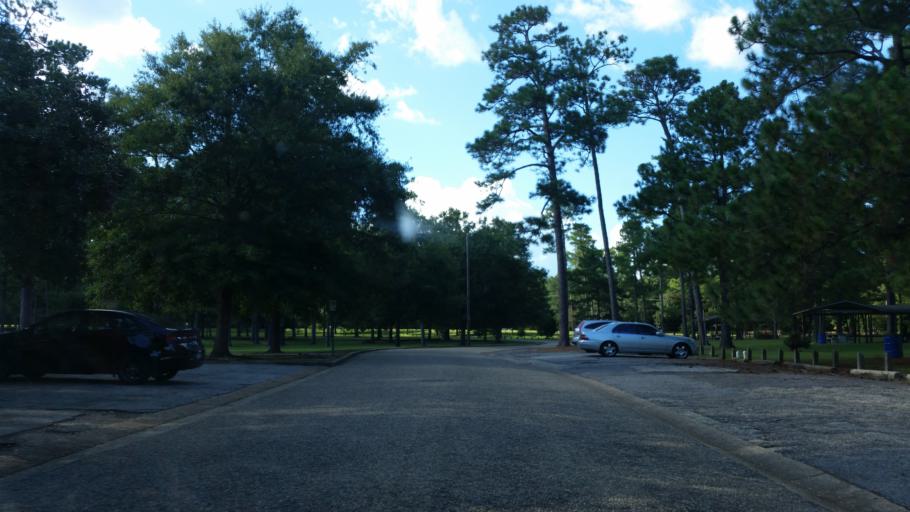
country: US
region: Alabama
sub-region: Mobile County
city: Prichard
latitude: 30.7071
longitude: -88.1559
